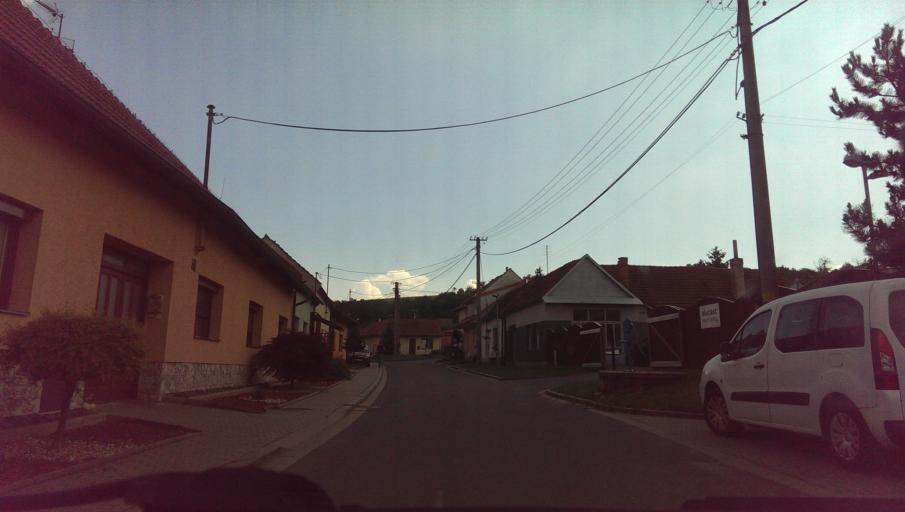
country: CZ
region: Zlin
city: Popovice
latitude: 49.0373
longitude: 17.5044
